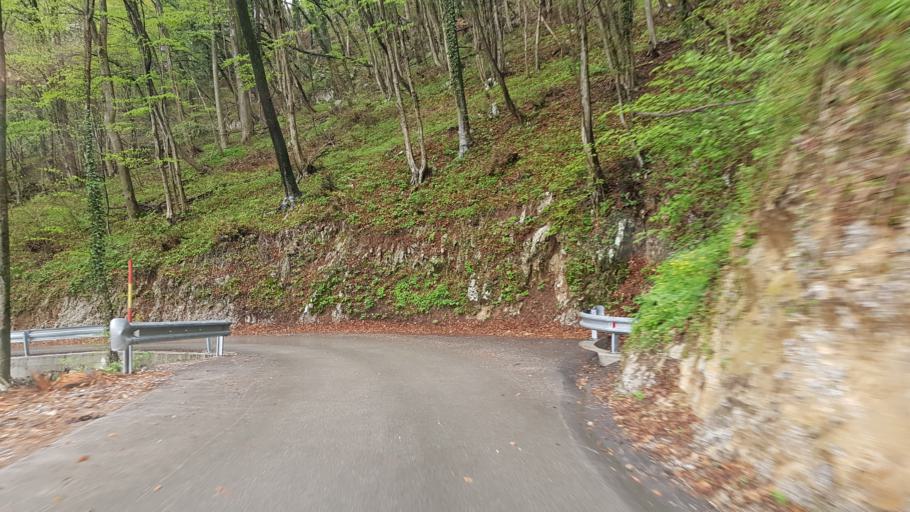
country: SI
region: Tolmin
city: Tolmin
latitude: 46.1466
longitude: 13.7801
